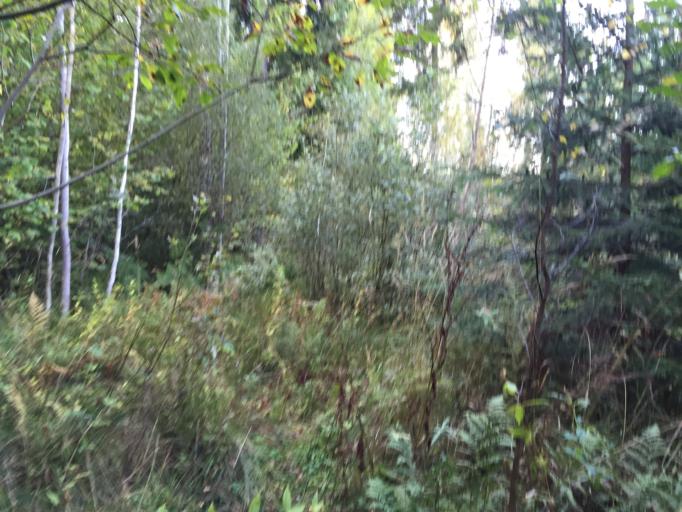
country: LV
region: Seja
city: Loja
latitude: 57.1293
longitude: 24.6179
